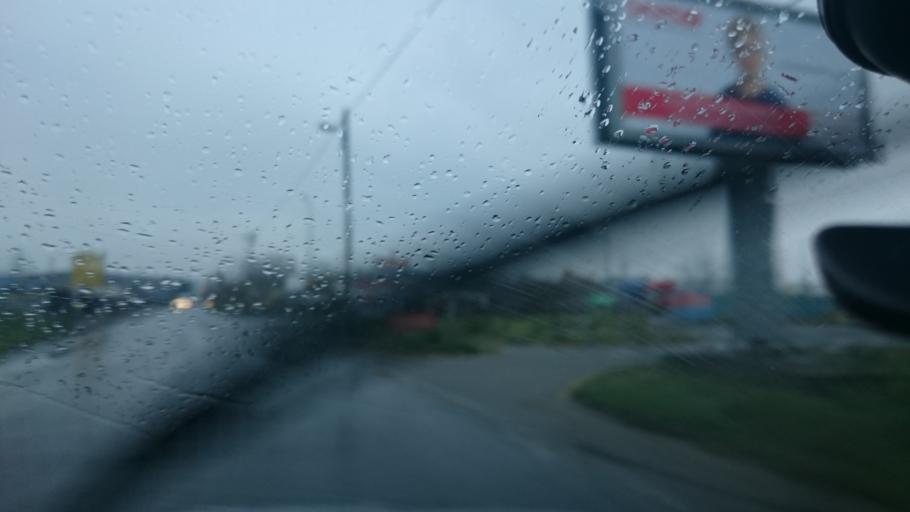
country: PL
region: Lesser Poland Voivodeship
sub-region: Powiat wielicki
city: Czarnochowice
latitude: 50.0309
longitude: 20.0406
